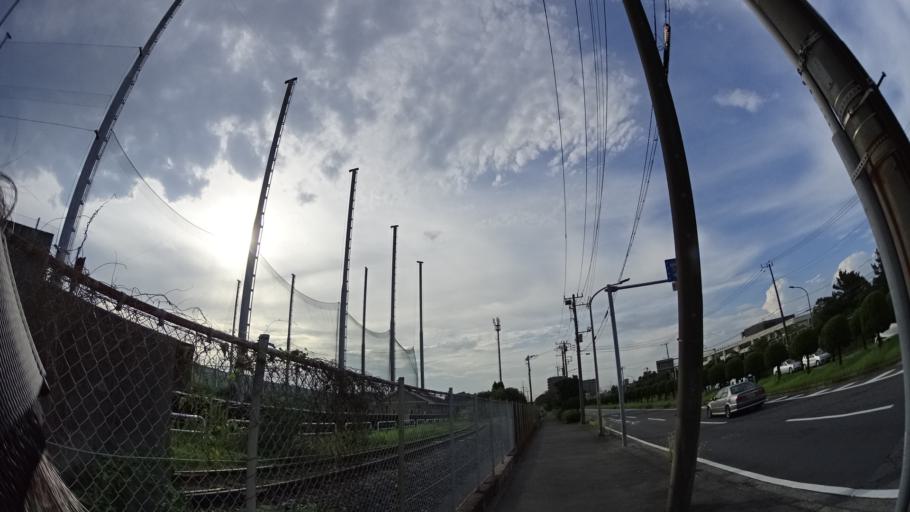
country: JP
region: Chiba
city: Funabashi
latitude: 35.6539
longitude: 140.0354
